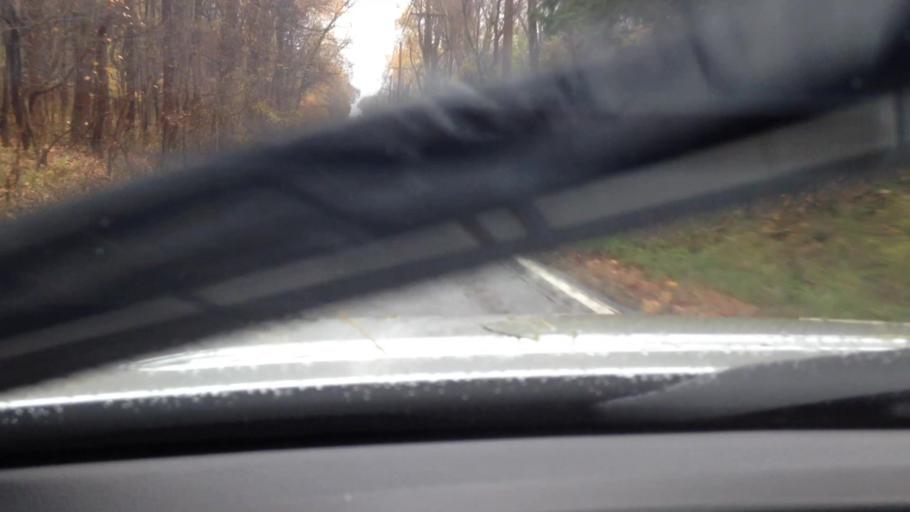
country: US
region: New York
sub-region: Orange County
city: Cornwall-on-Hudson
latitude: 41.4567
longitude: -73.9816
